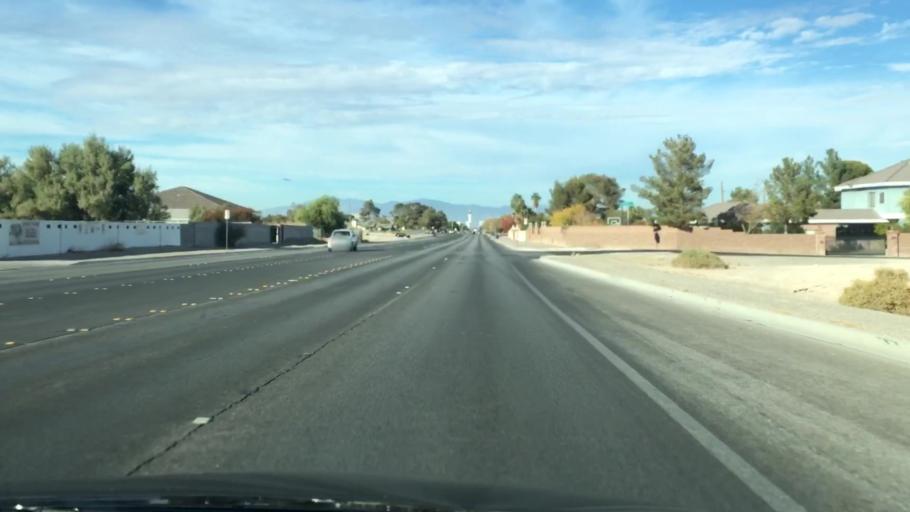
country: US
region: Nevada
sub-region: Clark County
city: Paradise
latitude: 36.0436
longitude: -115.1543
